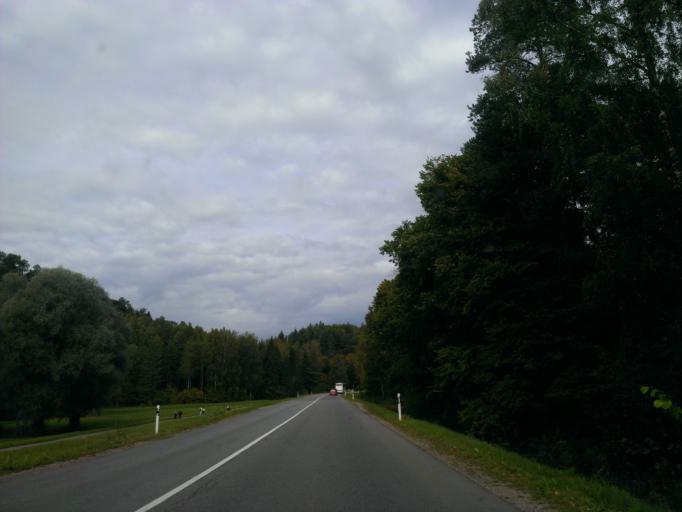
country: LV
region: Sigulda
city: Sigulda
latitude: 57.1680
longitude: 24.8384
